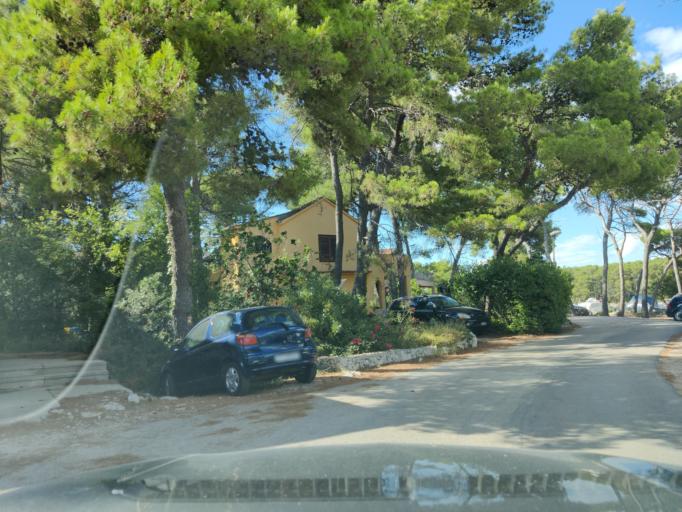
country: HR
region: Sibensko-Kniniska
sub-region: Grad Sibenik
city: Sibenik
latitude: 43.7249
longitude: 15.8472
